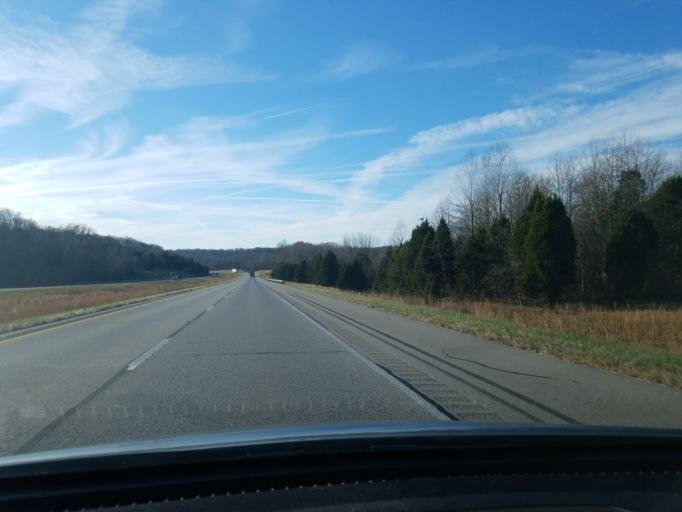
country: US
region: Indiana
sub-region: Harrison County
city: Corydon
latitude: 38.2545
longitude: -86.2991
